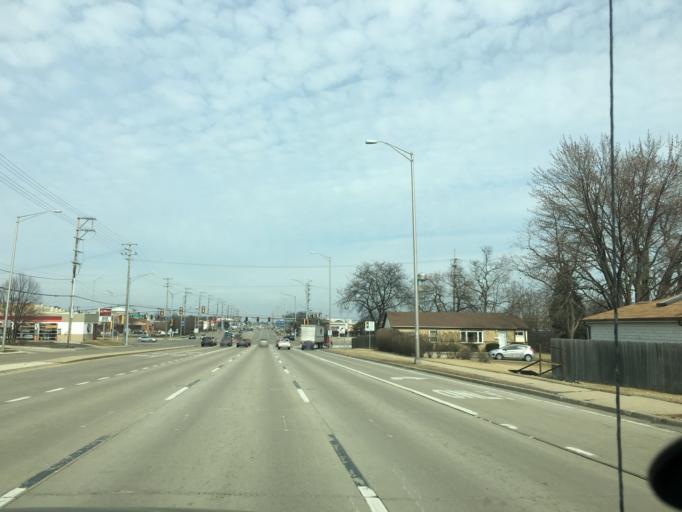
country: US
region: Illinois
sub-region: Cook County
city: Hoffman Estates
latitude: 42.0436
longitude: -88.0796
